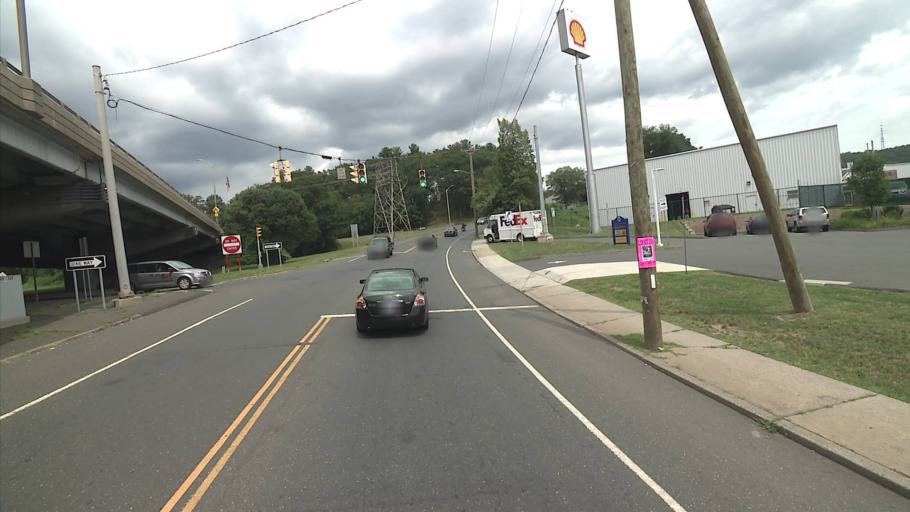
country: US
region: Connecticut
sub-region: New Haven County
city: Seymour
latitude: 41.3977
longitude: -73.0702
